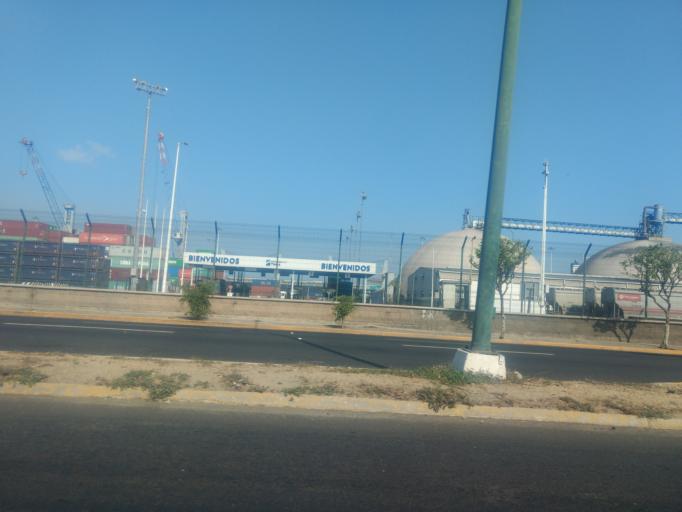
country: MX
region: Colima
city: Tapeixtles
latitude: 19.0614
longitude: -104.2901
